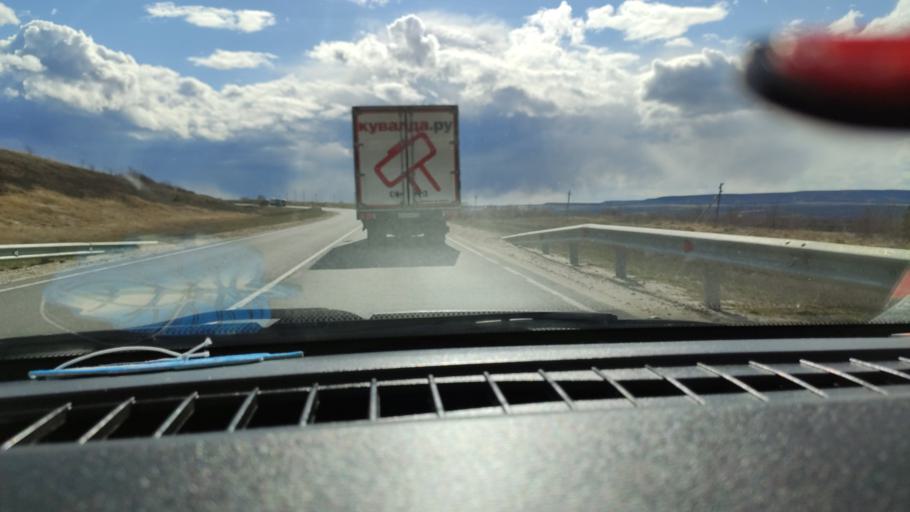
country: RU
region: Saratov
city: Alekseyevka
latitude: 52.3305
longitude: 47.9220
